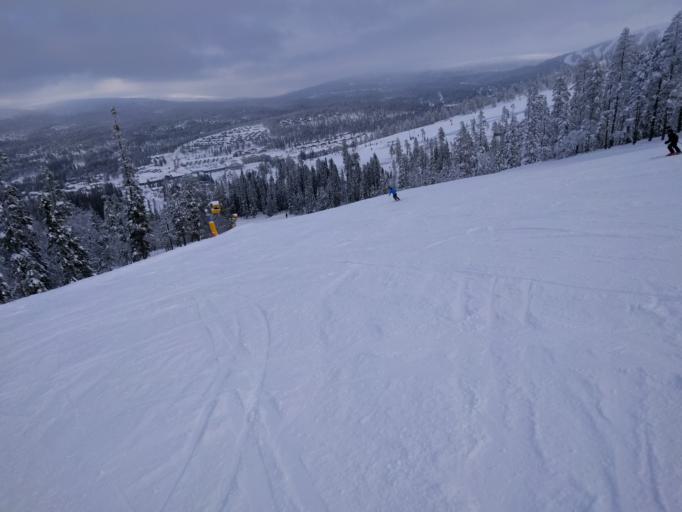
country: NO
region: Hedmark
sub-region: Trysil
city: Innbygda
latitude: 61.1707
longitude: 12.9554
